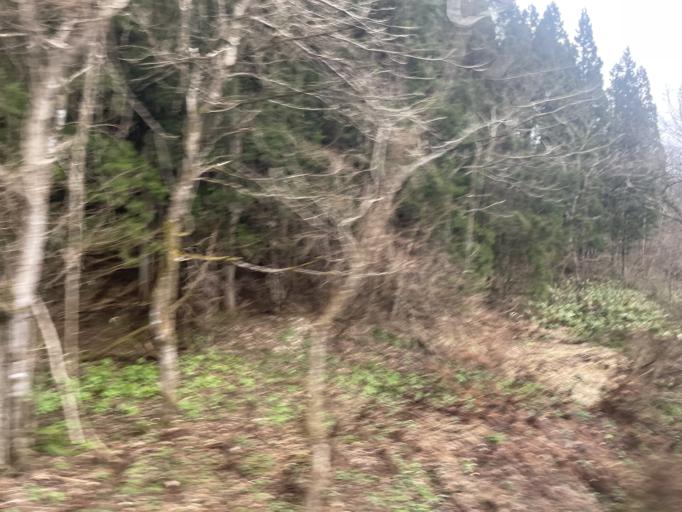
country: JP
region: Akita
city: Kakunodatemachi
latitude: 39.7232
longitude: 140.5556
